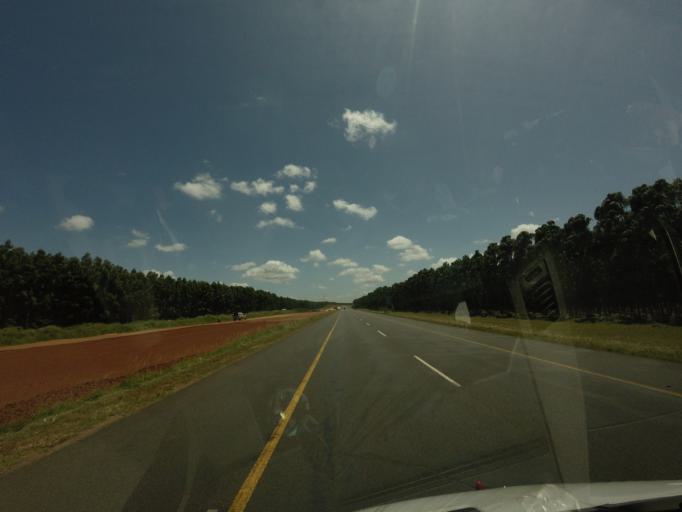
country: ZA
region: KwaZulu-Natal
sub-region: uThungulu District Municipality
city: Empangeni
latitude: -28.7477
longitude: 31.9369
